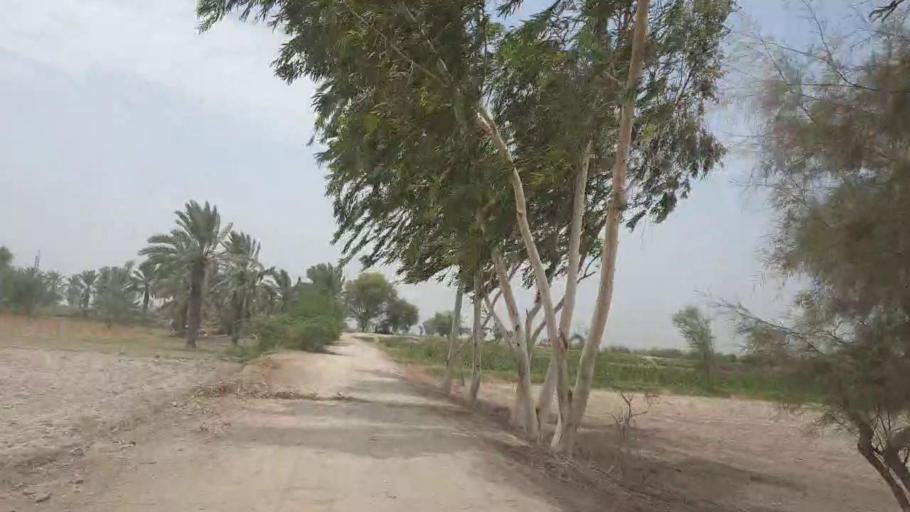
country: PK
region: Sindh
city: Kot Diji
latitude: 27.4436
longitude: 68.6780
